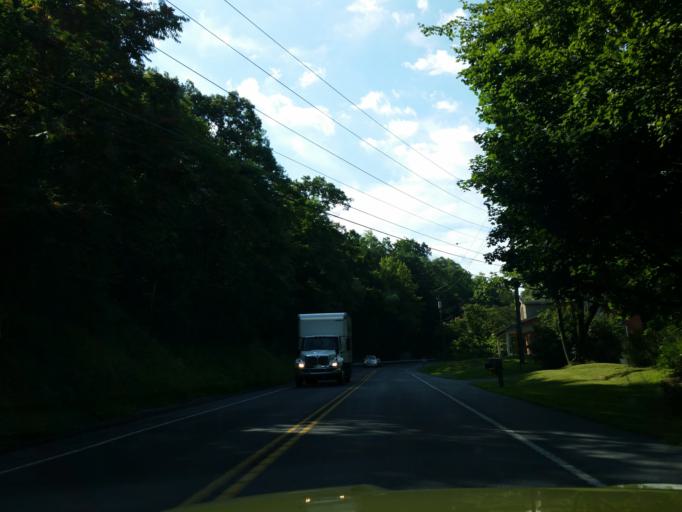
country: US
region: Pennsylvania
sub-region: Lebanon County
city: Sand Hill
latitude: 40.3935
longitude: -76.4155
